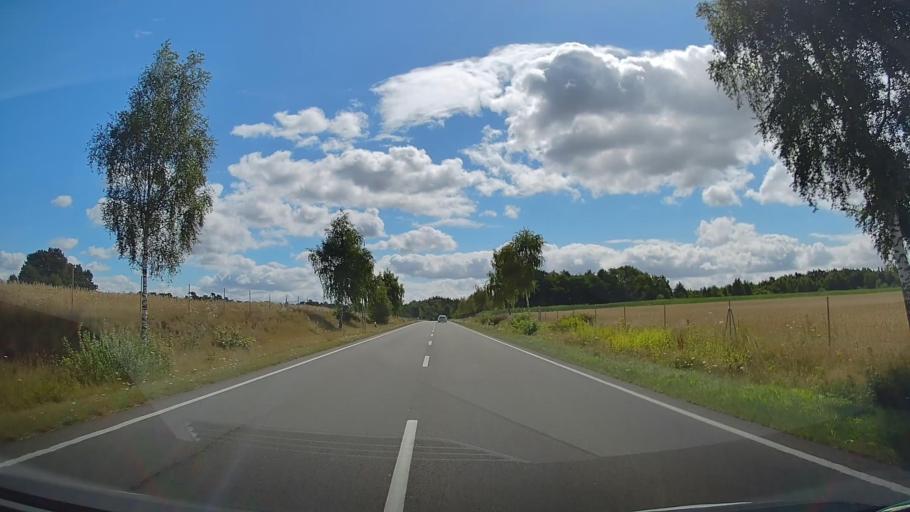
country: DE
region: Lower Saxony
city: Vechta
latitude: 52.7029
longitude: 8.2903
